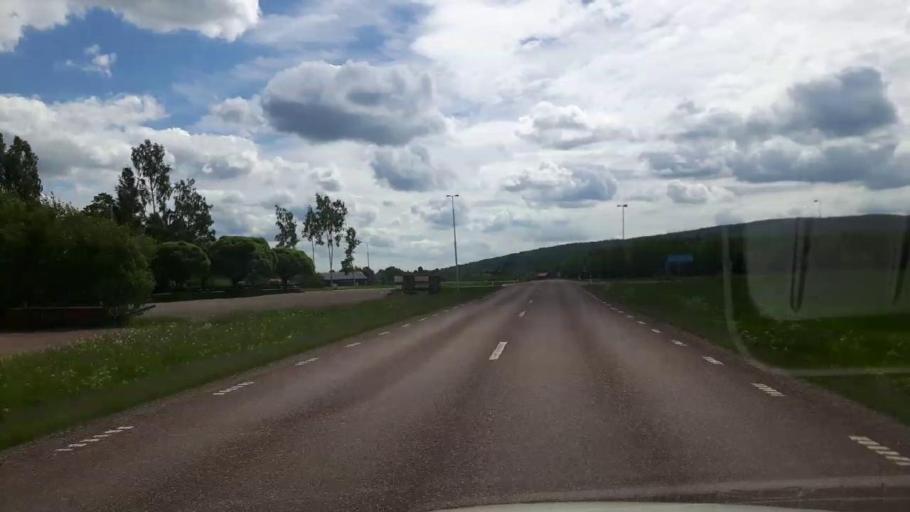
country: SE
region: Dalarna
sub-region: Saters Kommun
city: Saeter
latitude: 60.4032
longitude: 15.8734
